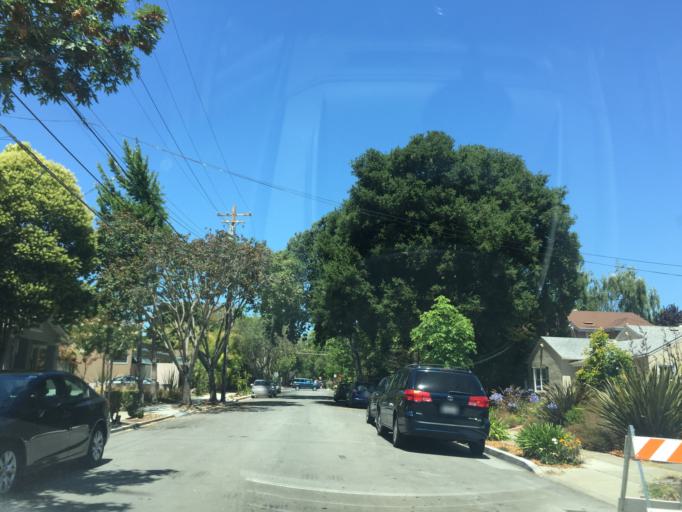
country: US
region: California
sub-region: Santa Clara County
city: Palo Alto
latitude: 37.4512
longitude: -122.1590
